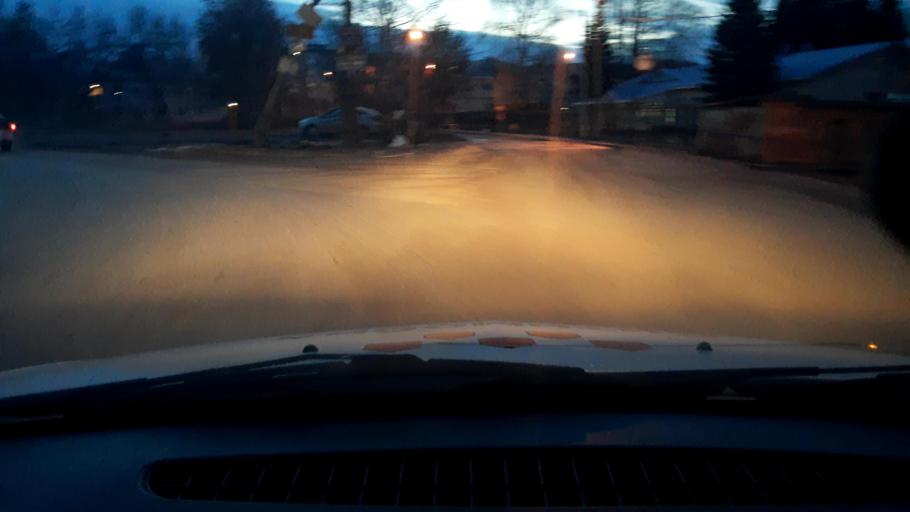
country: RU
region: Bashkortostan
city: Iglino
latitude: 54.7781
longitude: 56.2198
